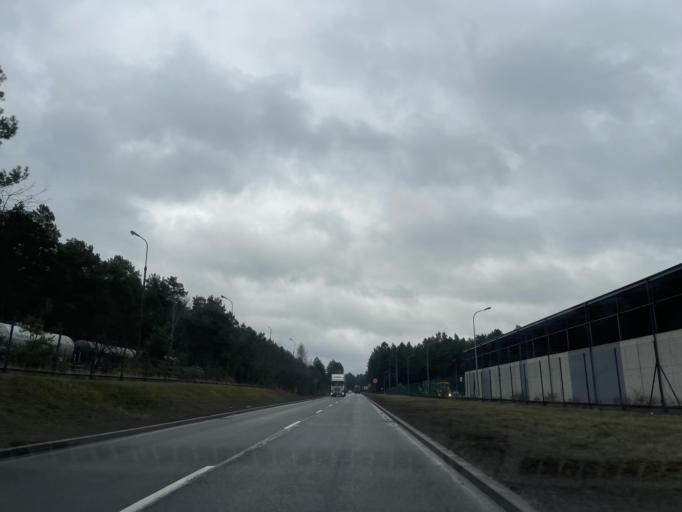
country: PL
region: Kujawsko-Pomorskie
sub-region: Bydgoszcz
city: Bydgoszcz
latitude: 53.0694
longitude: 18.0845
